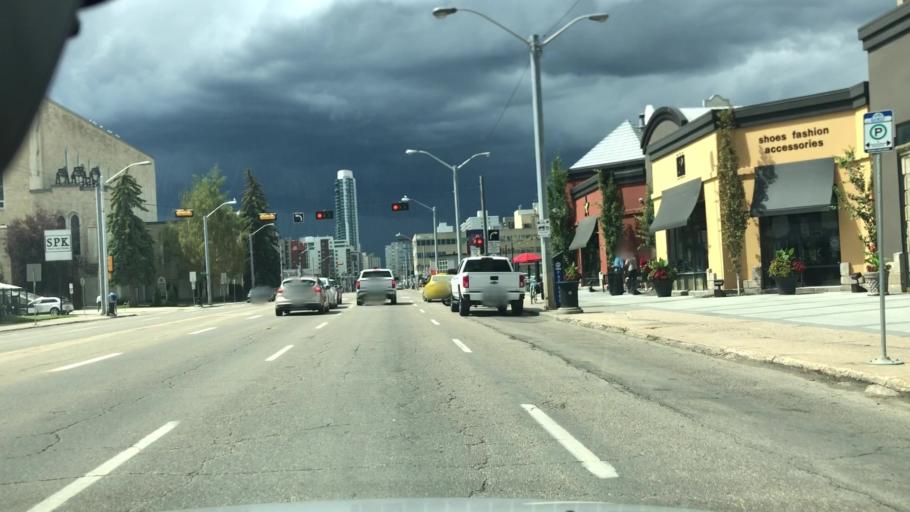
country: CA
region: Alberta
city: Edmonton
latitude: 53.5410
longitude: -113.5147
